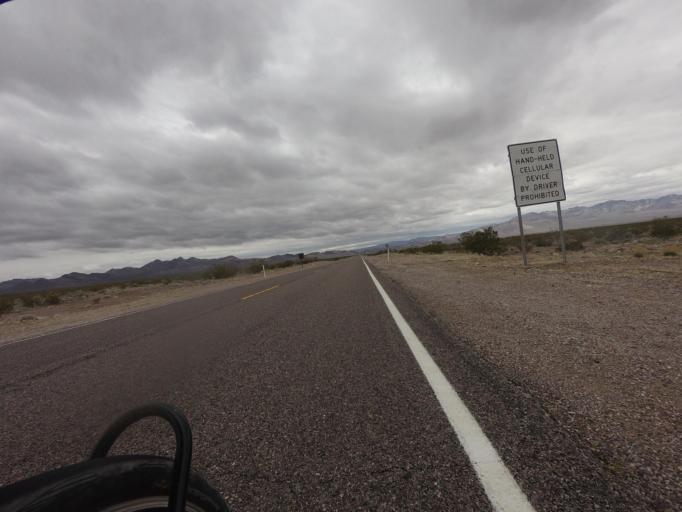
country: US
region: Nevada
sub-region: Nye County
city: Beatty
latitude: 36.8335
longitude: -116.8787
